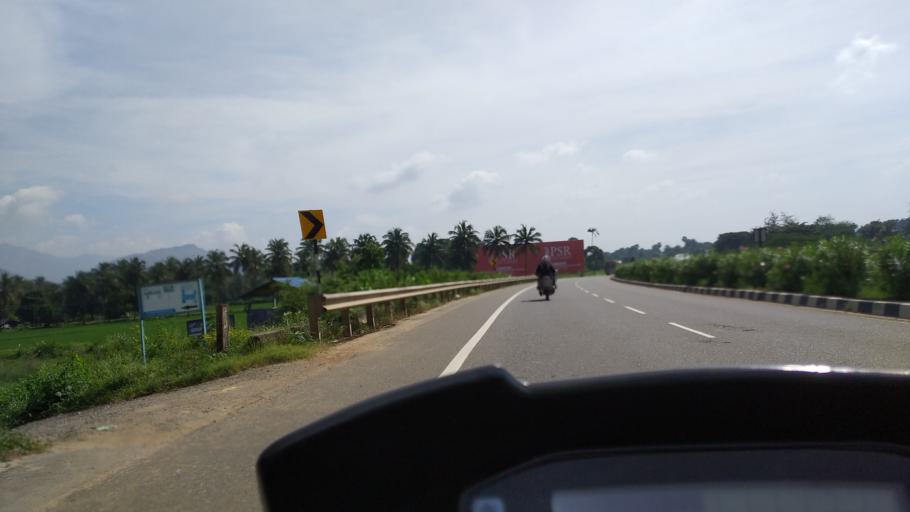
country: IN
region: Kerala
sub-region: Palakkad district
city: Chittur
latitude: 10.8163
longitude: 76.8018
